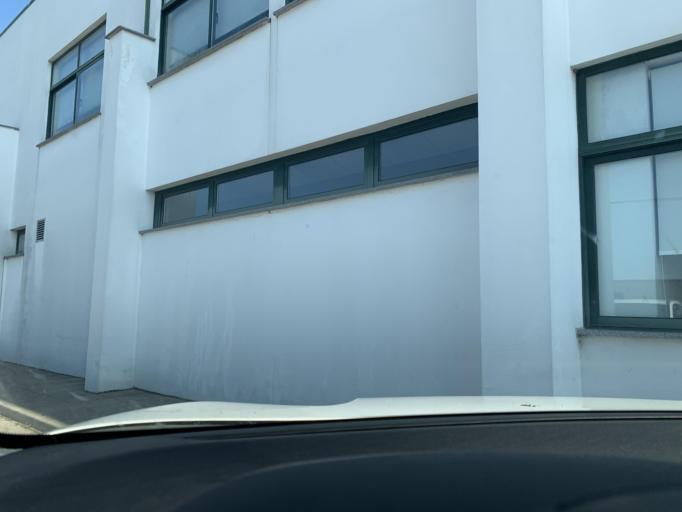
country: PT
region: Viseu
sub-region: Concelho de Tondela
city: Tondela
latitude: 40.4844
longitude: -8.0925
